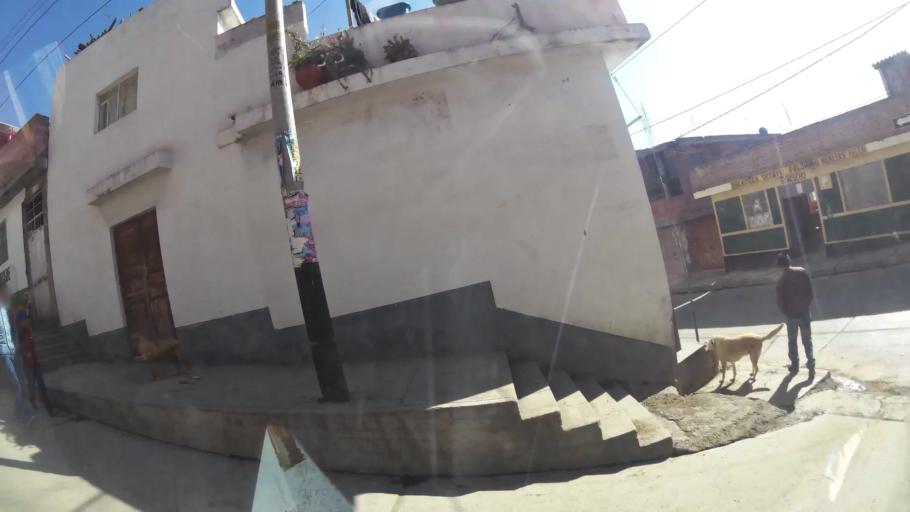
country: PE
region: Ayacucho
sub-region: Provincia de Huamanga
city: Ayacucho
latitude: -13.1624
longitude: -74.2311
